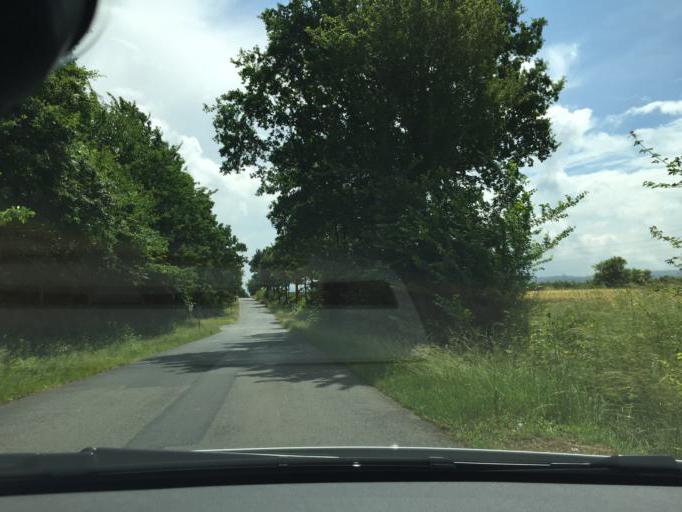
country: DE
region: Lower Saxony
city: Hehlen
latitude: 52.0339
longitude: 9.4018
